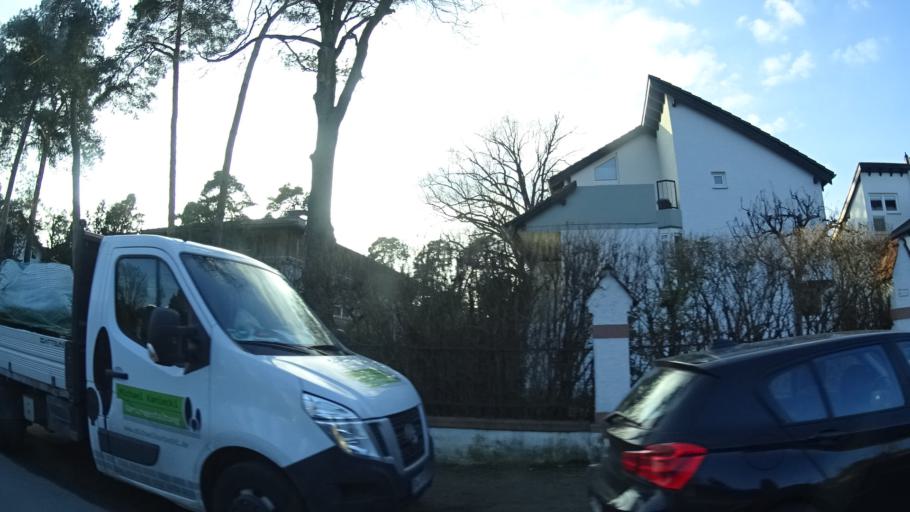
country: DE
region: Hesse
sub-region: Regierungsbezirk Darmstadt
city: Darmstadt
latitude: 49.8310
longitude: 8.6449
